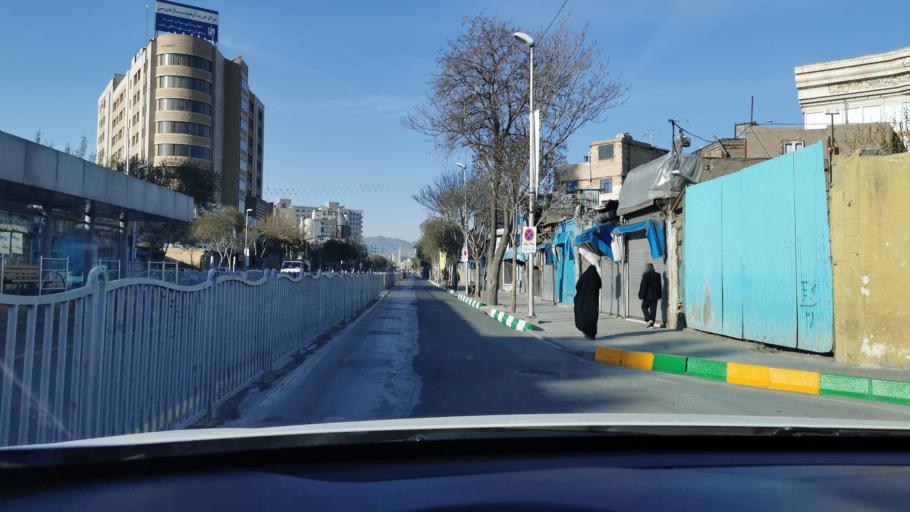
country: IR
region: Razavi Khorasan
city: Mashhad
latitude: 36.2954
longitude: 59.6274
